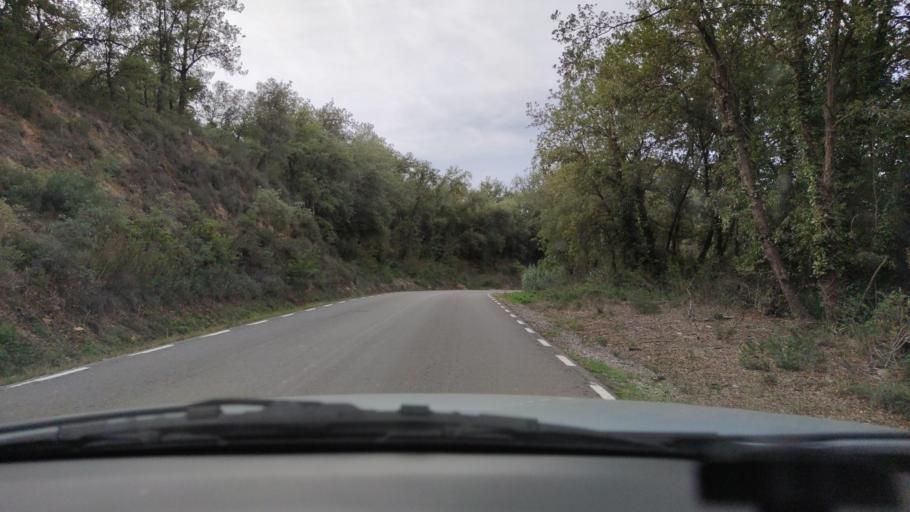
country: ES
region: Catalonia
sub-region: Provincia de Lleida
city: Artesa de Segre
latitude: 41.9133
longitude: 1.0772
